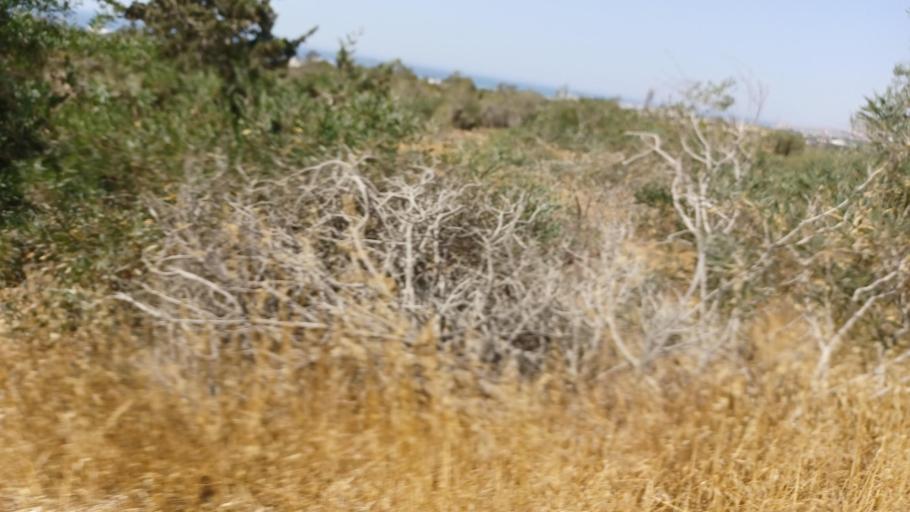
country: CY
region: Ammochostos
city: Ayia Napa
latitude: 35.0022
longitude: 33.9737
